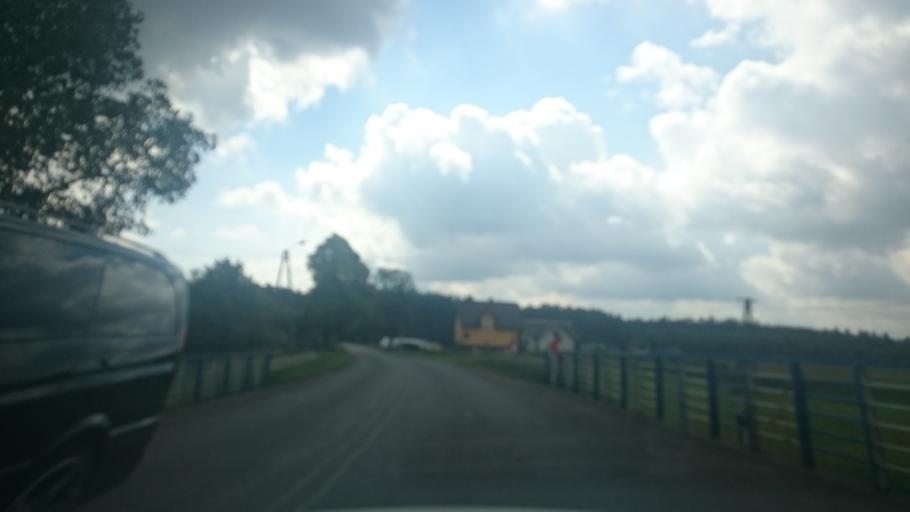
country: PL
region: Pomeranian Voivodeship
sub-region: Powiat koscierski
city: Stara Kiszewa
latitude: 53.9760
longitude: 18.2295
